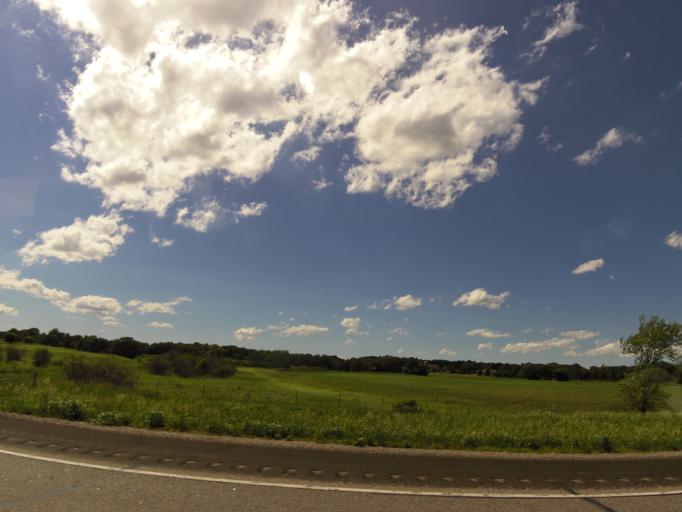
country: US
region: Minnesota
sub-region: Stearns County
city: Waite Park
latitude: 45.5090
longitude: -94.2311
